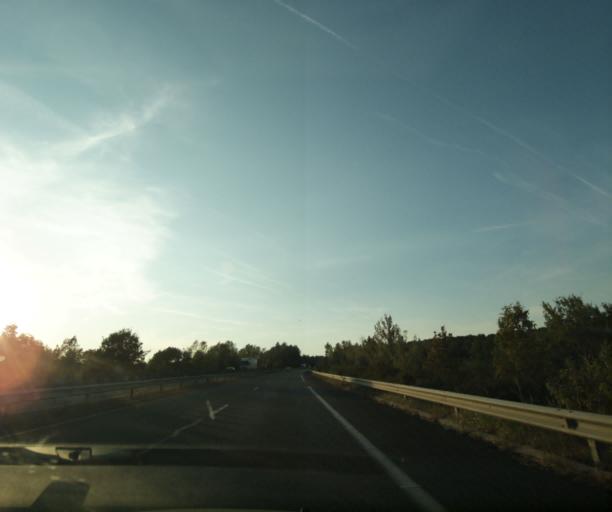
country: FR
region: Midi-Pyrenees
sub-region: Departement du Tarn-et-Garonne
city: Lamagistere
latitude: 44.0739
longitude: 0.8068
